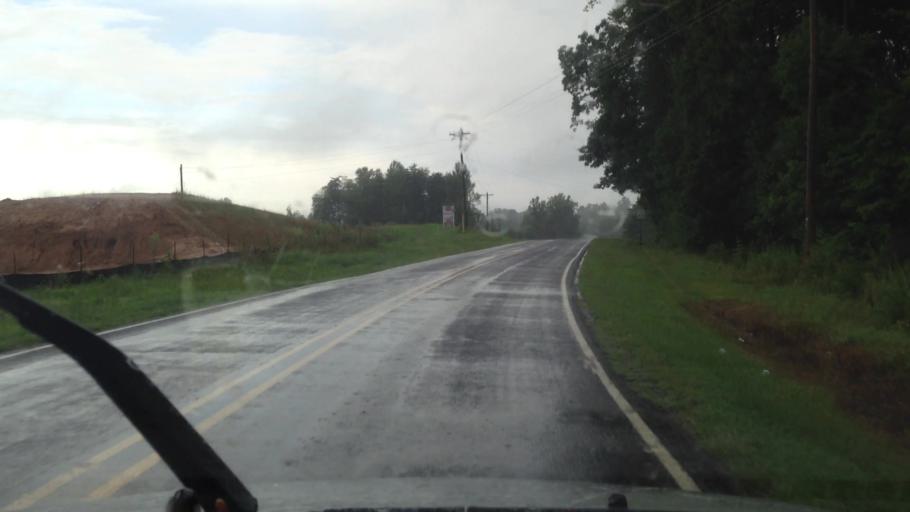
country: US
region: North Carolina
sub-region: Guilford County
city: Oak Ridge
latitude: 36.2115
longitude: -80.0284
